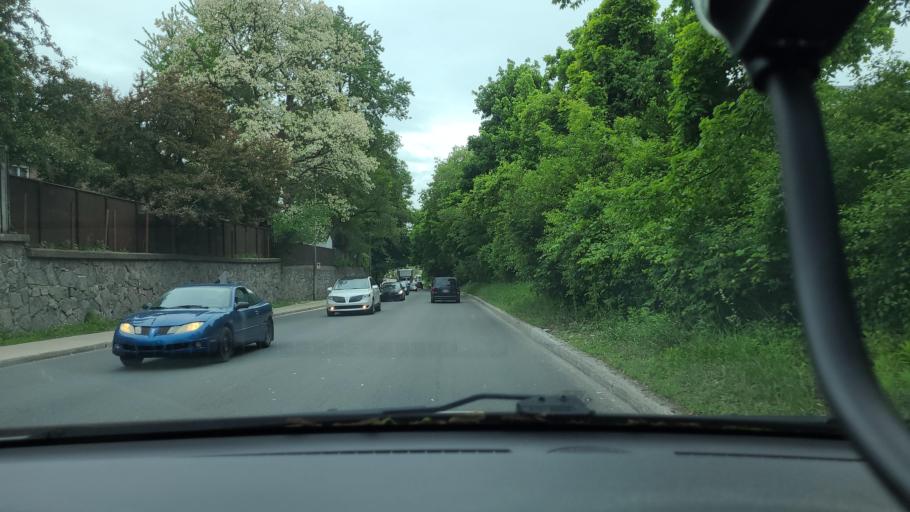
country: CA
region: Quebec
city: Montreal-Ouest
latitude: 45.4509
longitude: -73.6420
